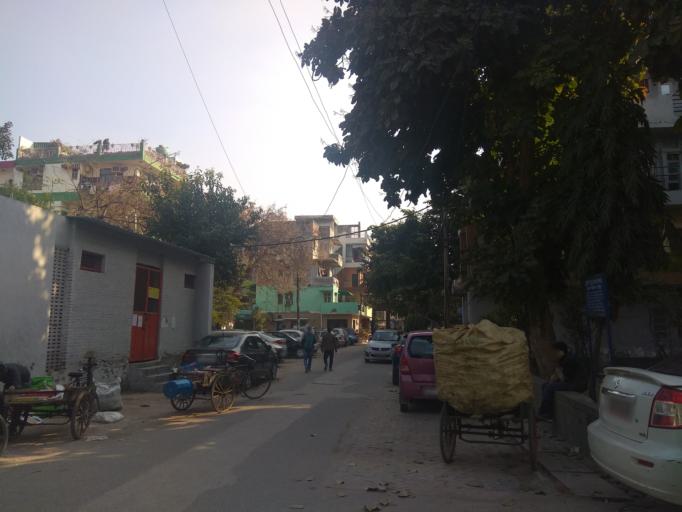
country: IN
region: NCT
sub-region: West Delhi
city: Nangloi Jat
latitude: 28.6266
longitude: 77.0670
